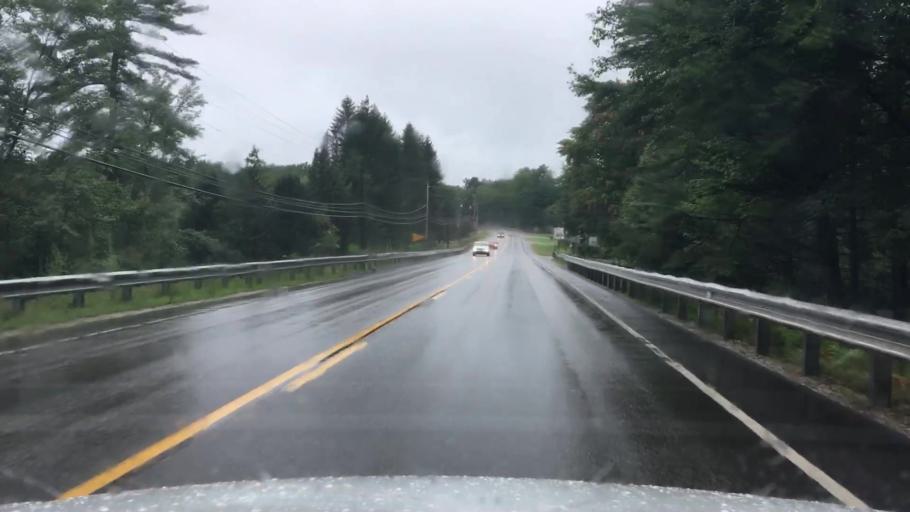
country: US
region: Maine
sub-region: Oxford County
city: Fryeburg
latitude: 43.9979
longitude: -71.0208
